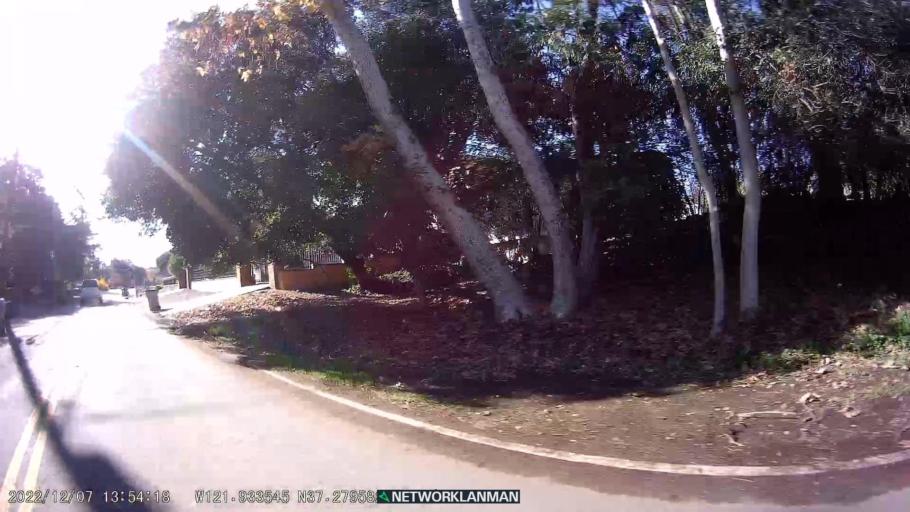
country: US
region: California
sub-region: Santa Clara County
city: Campbell
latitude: 37.2793
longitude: -121.9336
